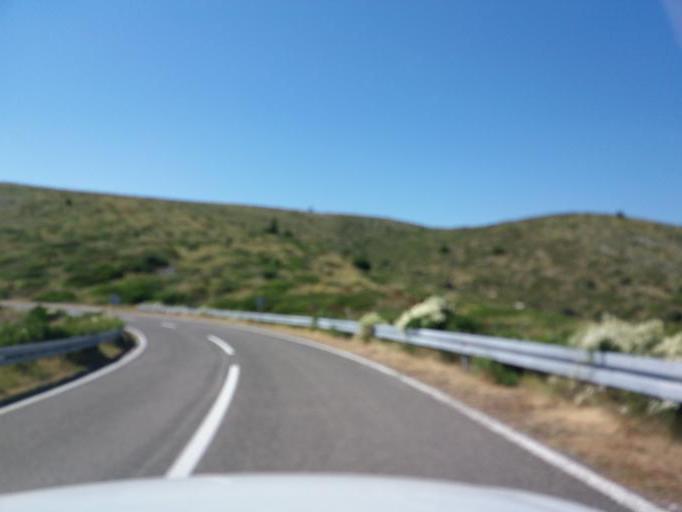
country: HR
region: Zadarska
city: Ugljan
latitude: 44.0371
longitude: 15.0201
